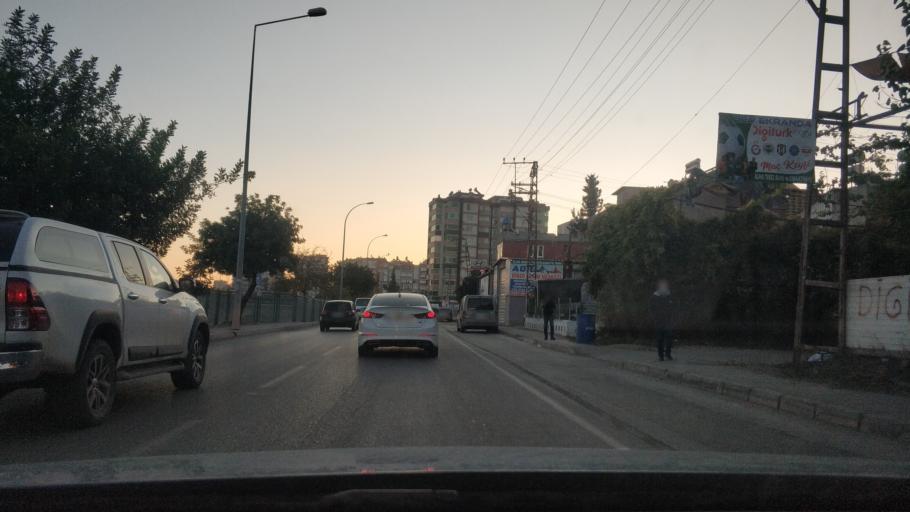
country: TR
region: Adana
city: Seyhan
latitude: 37.0105
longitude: 35.2981
